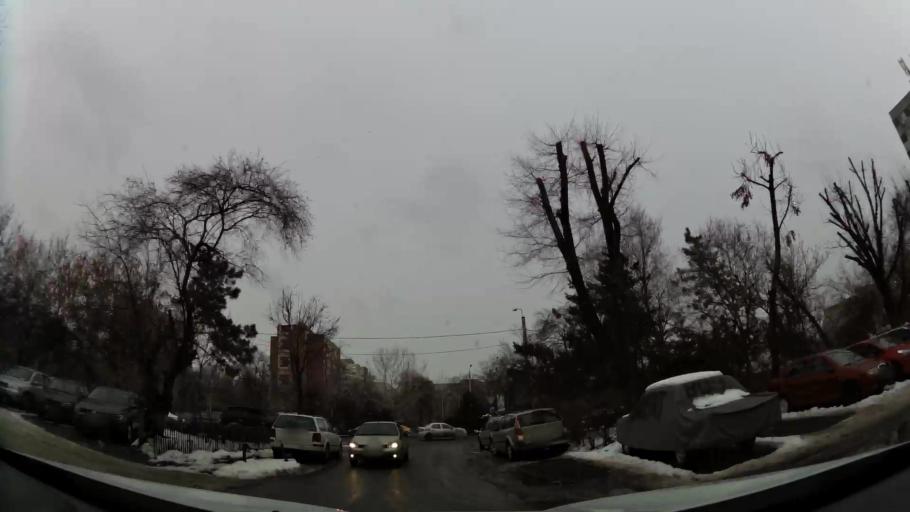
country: RO
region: Ilfov
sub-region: Comuna Chiajna
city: Rosu
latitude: 44.4235
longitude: 26.0453
